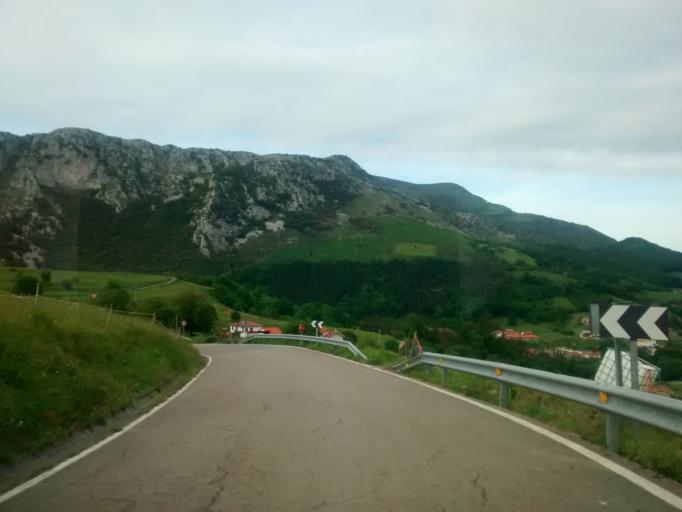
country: ES
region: Cantabria
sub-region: Provincia de Cantabria
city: San Vicente de la Barquera
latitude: 43.2519
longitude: -4.4175
